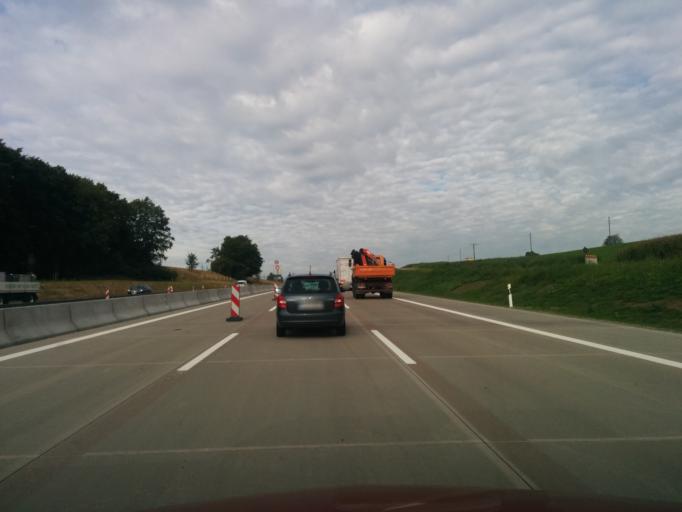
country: DE
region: Bavaria
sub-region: Swabia
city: Rettenbach
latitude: 48.4322
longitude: 10.3519
